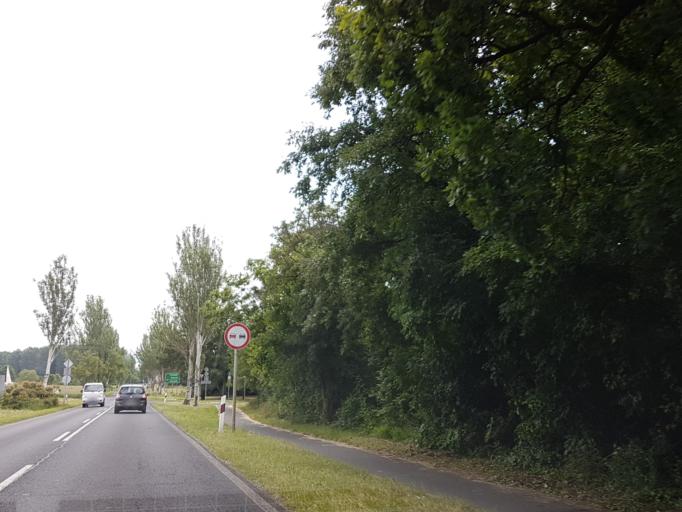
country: HU
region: Veszprem
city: Revfueloep
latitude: 46.8291
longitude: 17.5996
